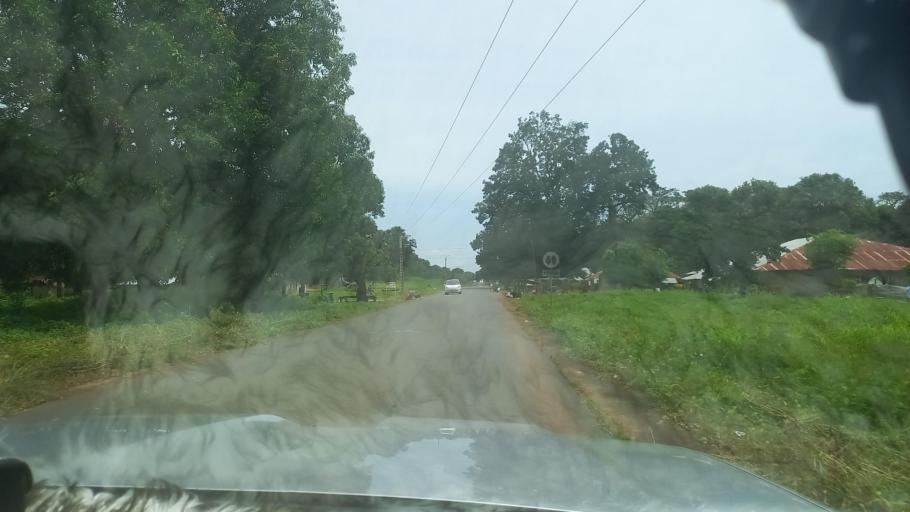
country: SN
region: Kolda
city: Marsassoum
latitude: 12.9594
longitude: -15.9980
